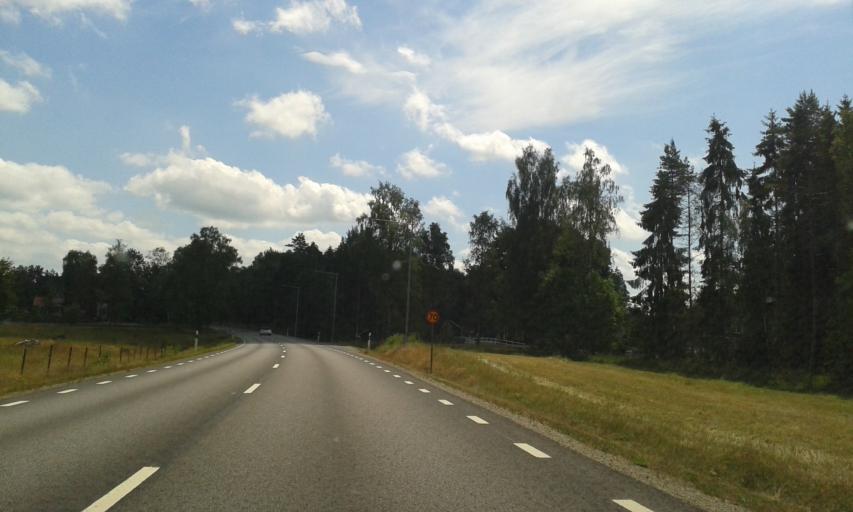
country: SE
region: Kronoberg
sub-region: Alvesta Kommun
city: Vislanda
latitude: 56.9099
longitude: 14.4274
